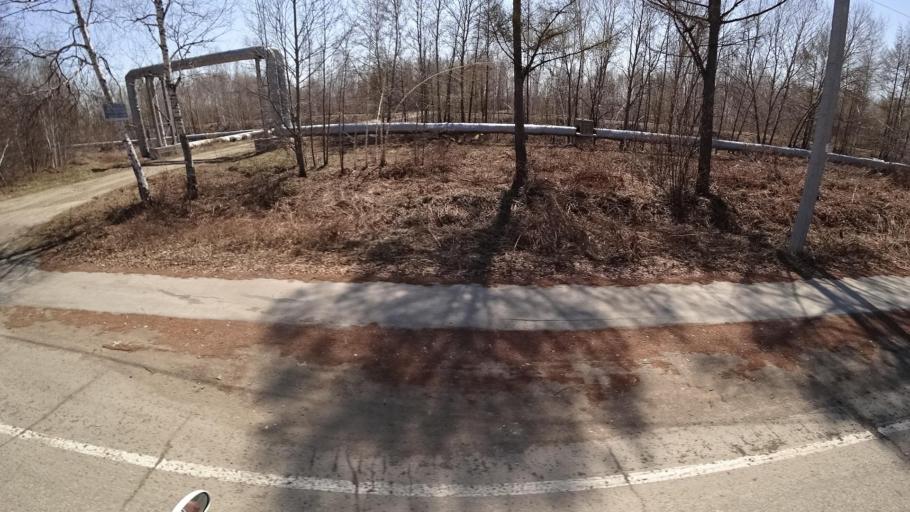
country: RU
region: Khabarovsk Krai
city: Khurba
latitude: 50.4055
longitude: 136.9000
